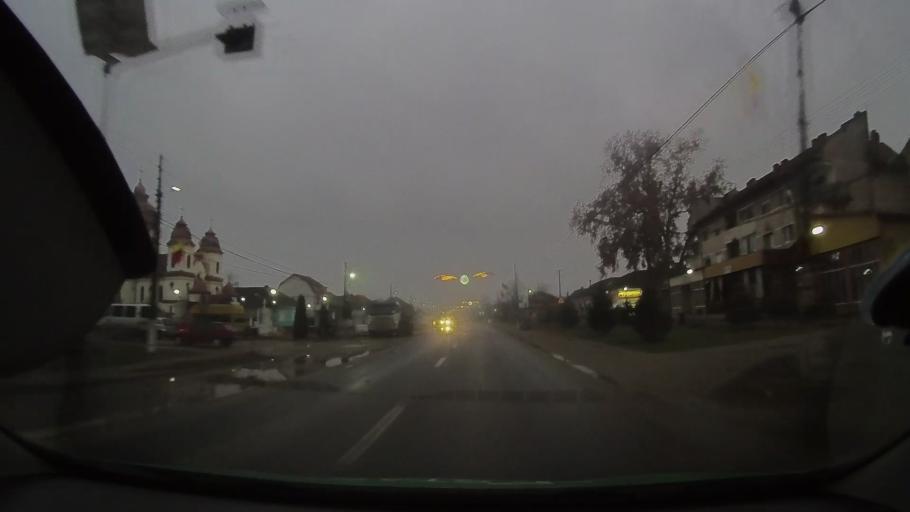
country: RO
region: Arad
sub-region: Comuna Beliu
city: Beliu
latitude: 46.4918
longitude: 21.9854
